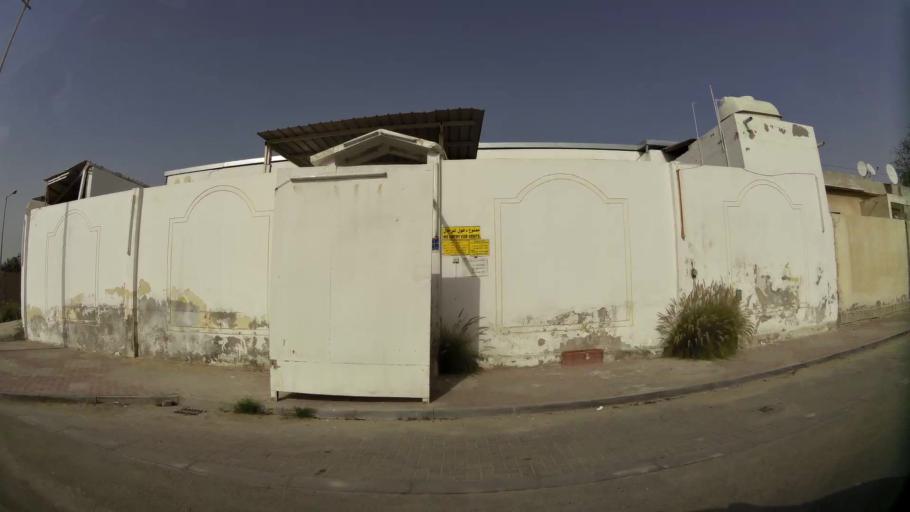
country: QA
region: Baladiyat ar Rayyan
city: Ar Rayyan
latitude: 25.2394
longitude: 51.4405
